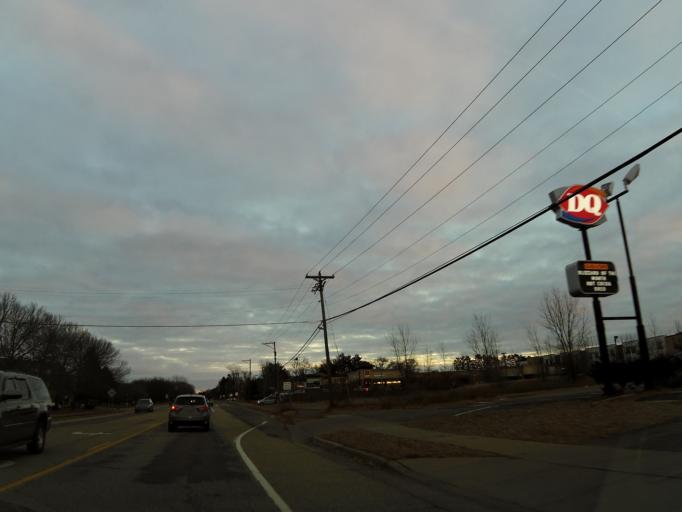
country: US
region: Minnesota
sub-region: Washington County
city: Birchwood
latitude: 45.0502
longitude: -92.9826
